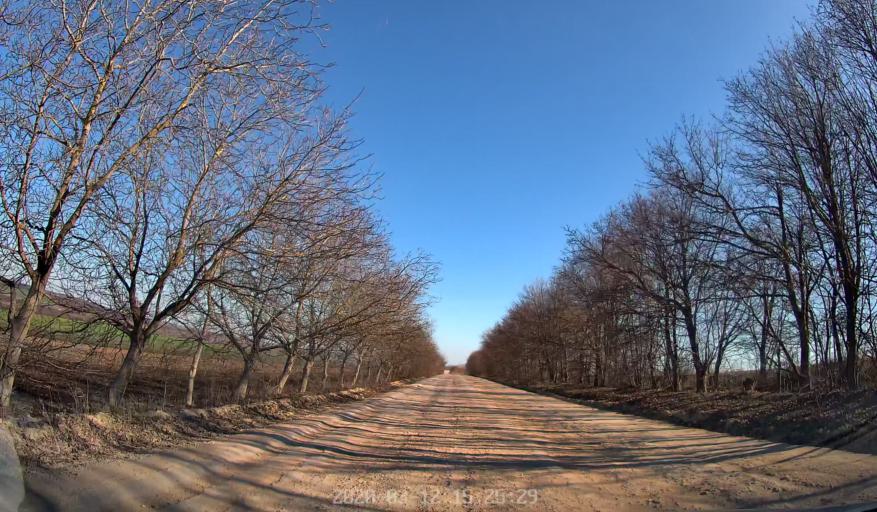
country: MD
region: Chisinau
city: Ciorescu
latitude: 47.1823
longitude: 28.9188
